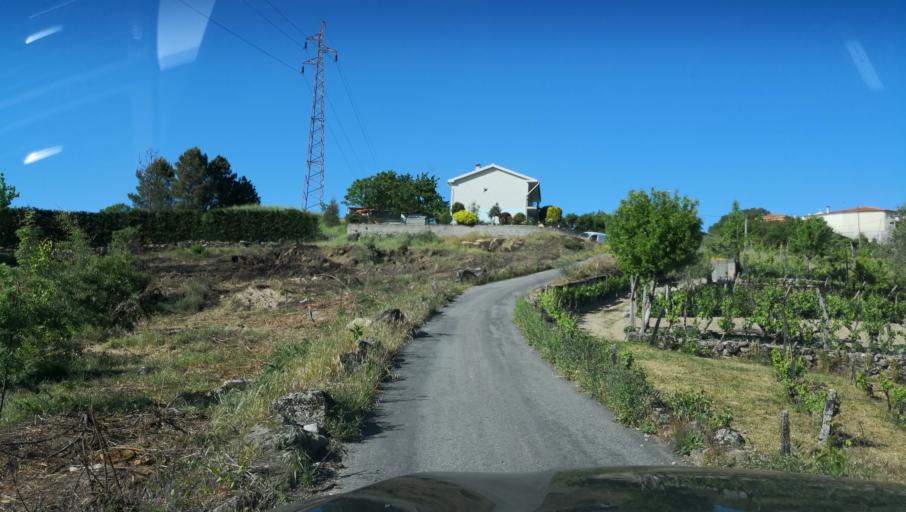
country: PT
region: Vila Real
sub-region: Vila Real
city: Vila Real
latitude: 41.3307
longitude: -7.7323
